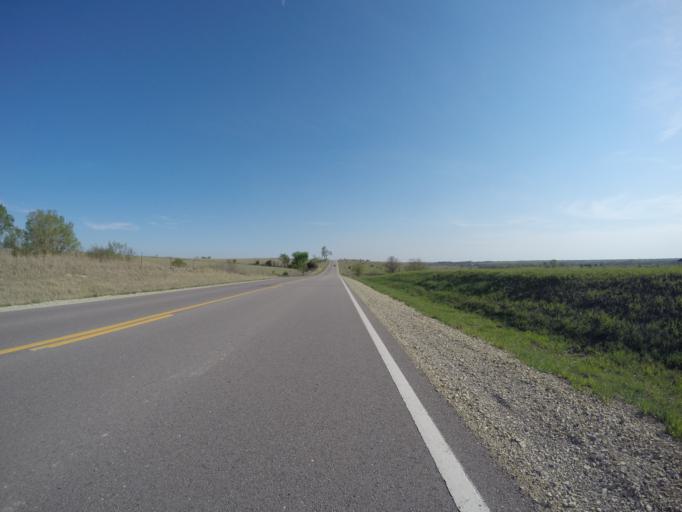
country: US
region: Kansas
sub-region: Riley County
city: Fort Riley North
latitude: 39.2749
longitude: -96.7751
